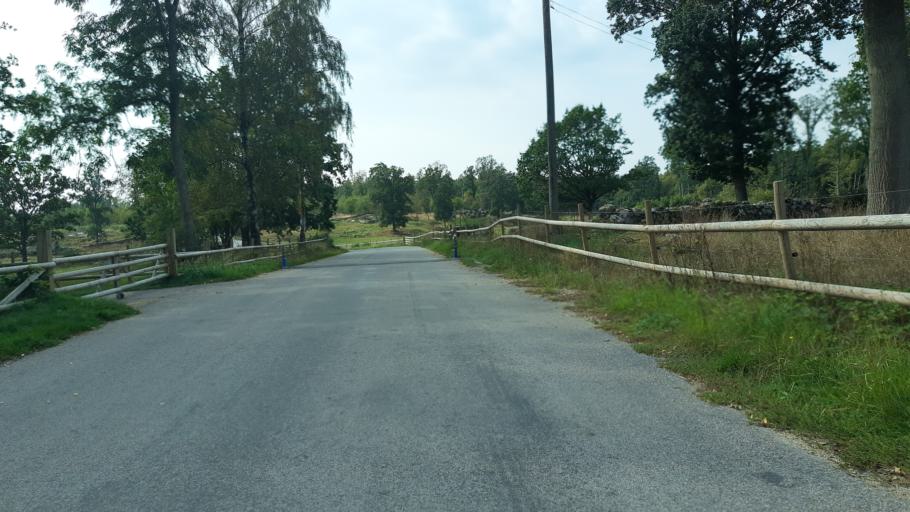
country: SE
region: Blekinge
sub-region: Karlskrona Kommun
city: Nattraby
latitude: 56.1810
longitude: 15.4961
